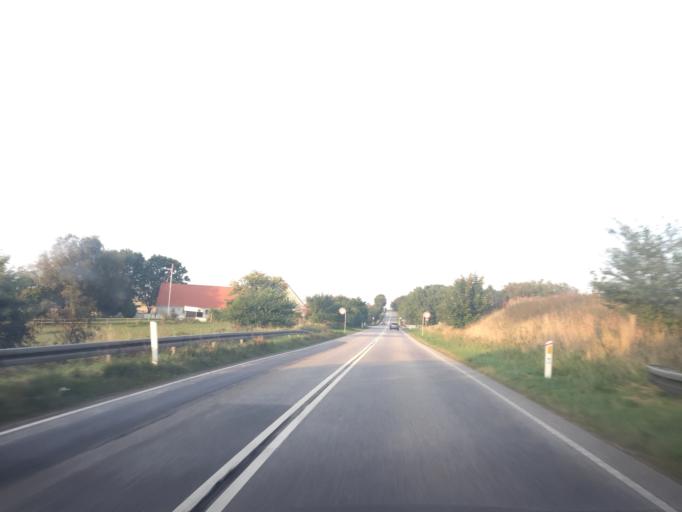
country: DK
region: Zealand
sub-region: Lejre Kommune
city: Kirke Hvalso
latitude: 55.5817
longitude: 11.8492
